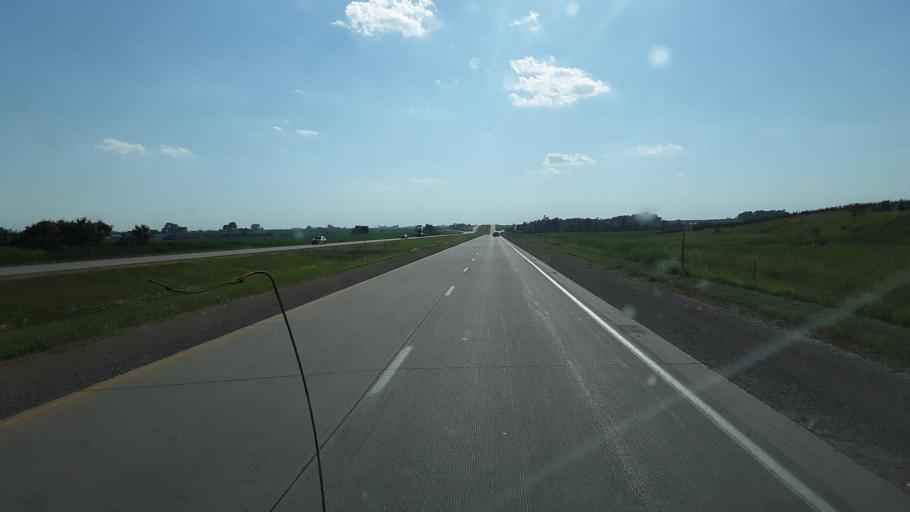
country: US
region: Iowa
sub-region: Grundy County
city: Grundy Center
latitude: 42.4631
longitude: -92.7501
